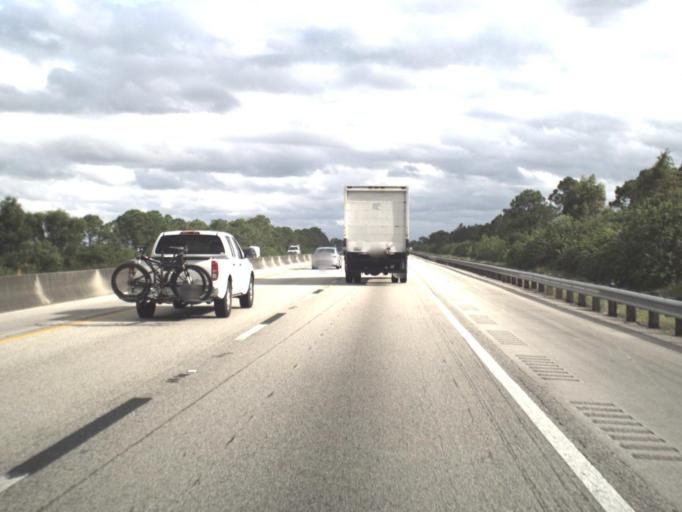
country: US
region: Florida
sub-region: Palm Beach County
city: Tequesta
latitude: 26.9980
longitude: -80.2002
